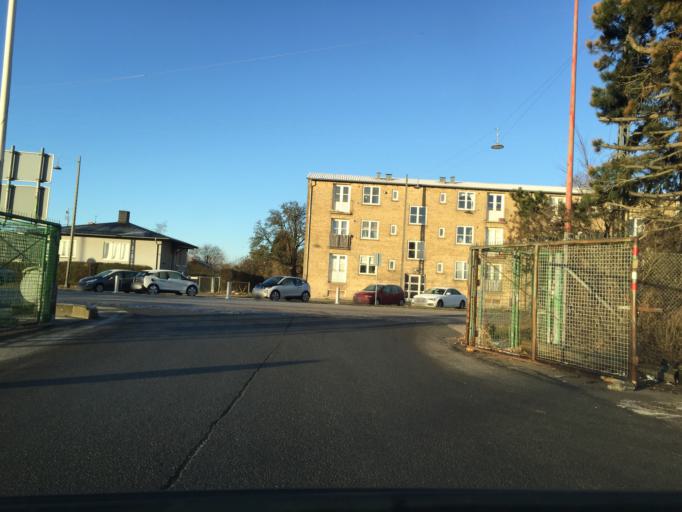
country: DK
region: Capital Region
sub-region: Hvidovre Kommune
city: Hvidovre
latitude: 55.6558
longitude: 12.5014
